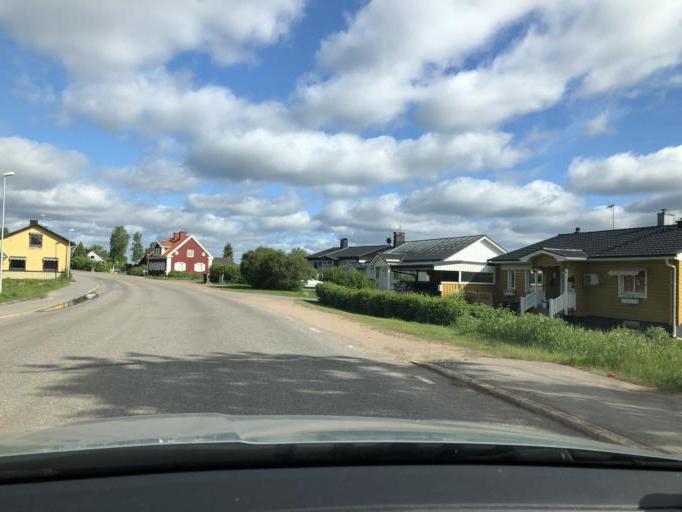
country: SE
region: Norrbotten
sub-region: Pajala Kommun
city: Pajala
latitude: 67.2150
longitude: 23.3663
